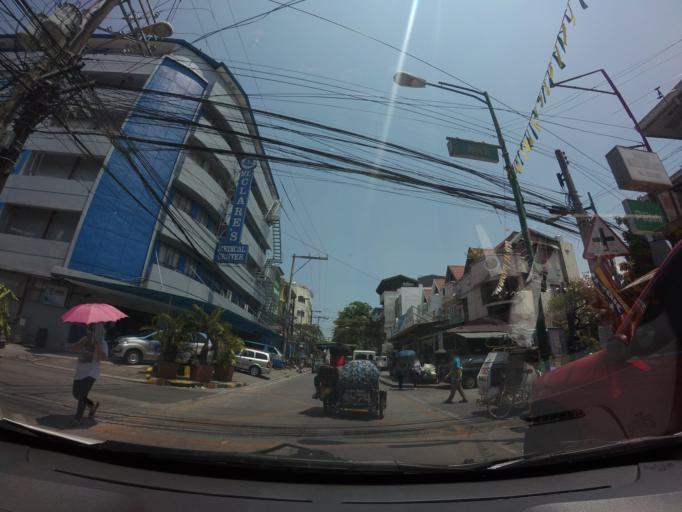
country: PH
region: Metro Manila
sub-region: Makati City
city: Makati City
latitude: 14.5629
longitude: 121.0016
